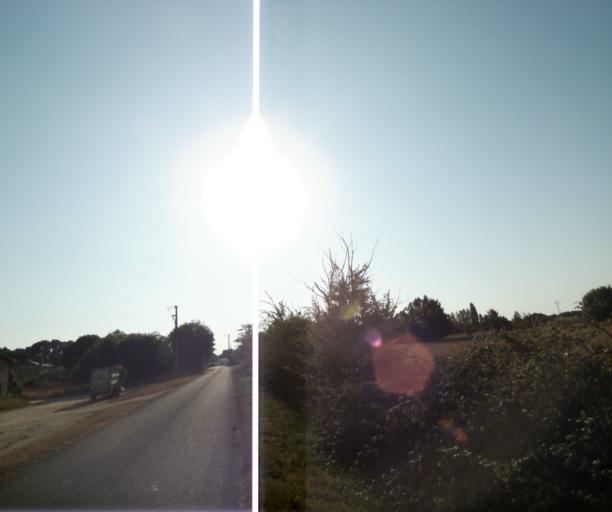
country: FR
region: Poitou-Charentes
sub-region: Departement de la Charente-Maritime
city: Muron
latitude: 45.9844
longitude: -0.8233
